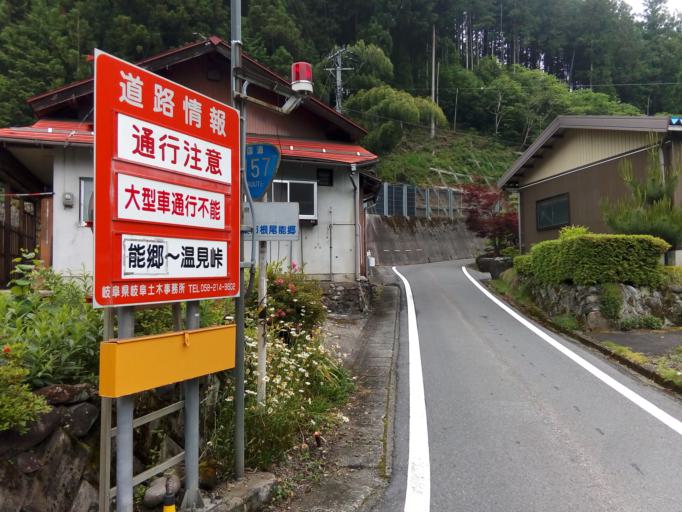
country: JP
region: Gifu
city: Godo
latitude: 35.6856
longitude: 136.5694
